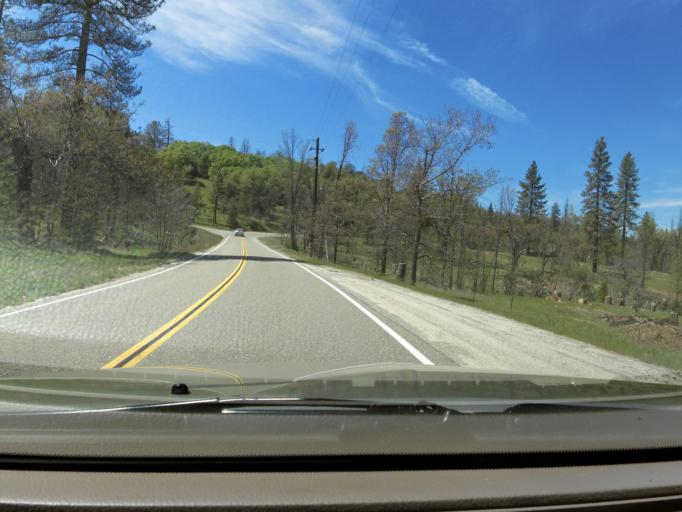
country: US
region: California
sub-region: Madera County
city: Oakhurst
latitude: 37.2554
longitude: -119.5682
